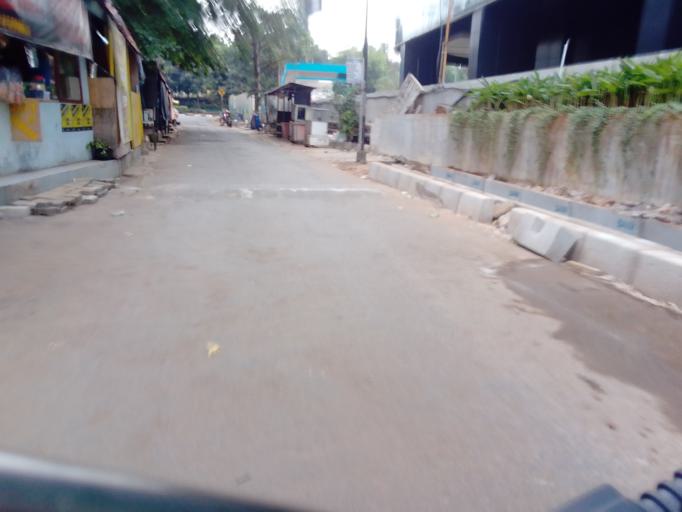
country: ID
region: Jakarta Raya
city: Jakarta
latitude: -6.2043
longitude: 106.8024
